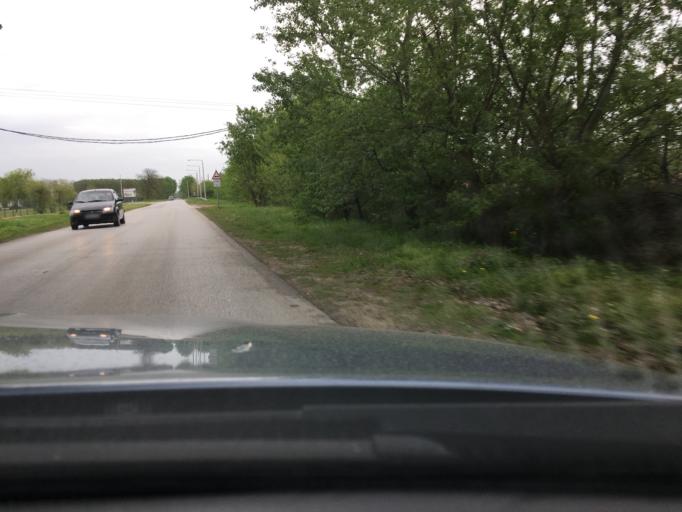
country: HU
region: Hajdu-Bihar
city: Debrecen
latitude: 47.5487
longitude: 21.6856
